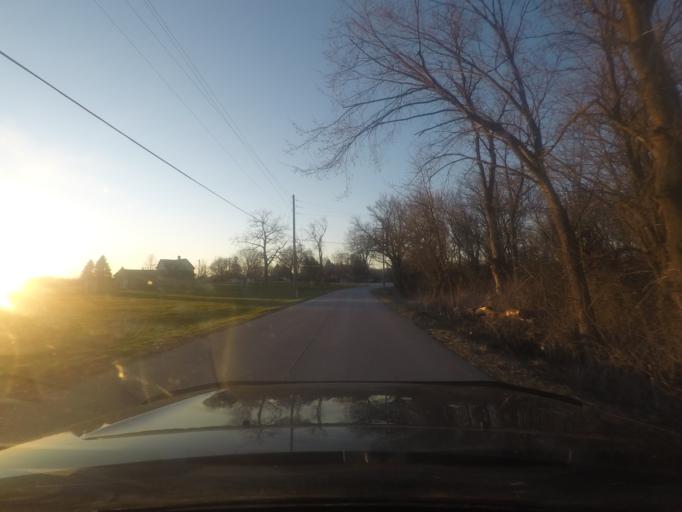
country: US
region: Indiana
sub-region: LaPorte County
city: Kingsford Heights
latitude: 41.5165
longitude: -86.7012
